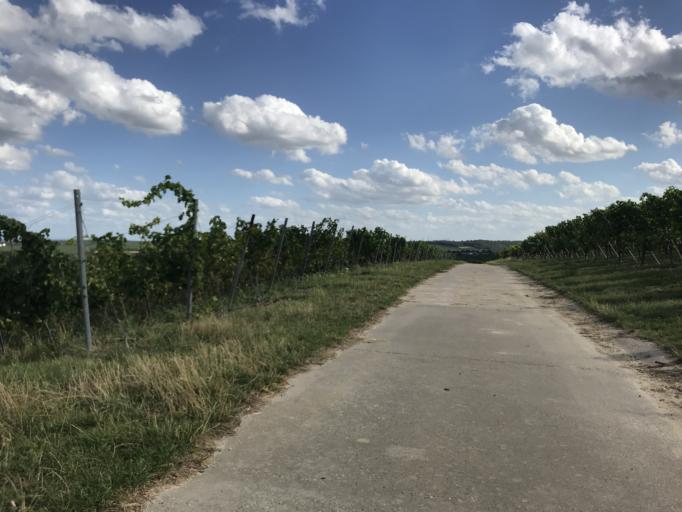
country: DE
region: Rheinland-Pfalz
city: Bodenheim
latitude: 49.9388
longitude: 8.2980
